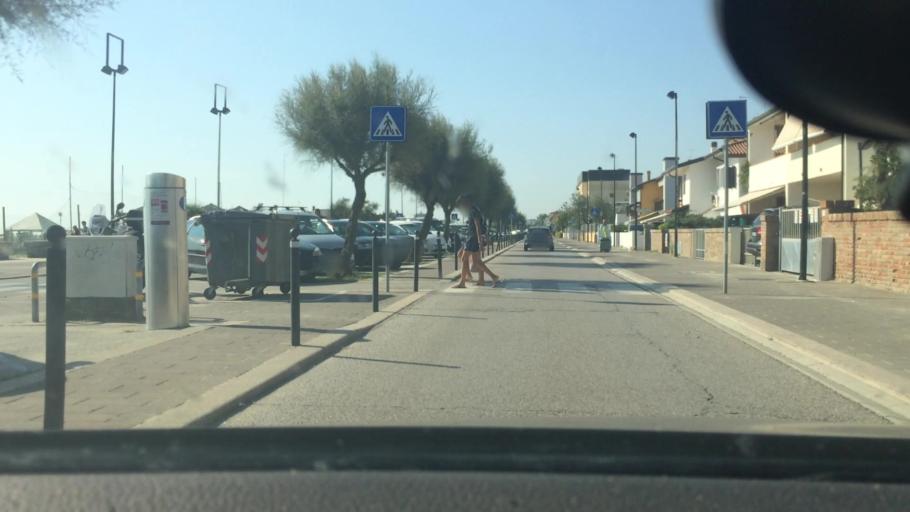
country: IT
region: Emilia-Romagna
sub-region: Provincia di Ferrara
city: Porto Garibaldi
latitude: 44.6851
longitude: 12.2404
